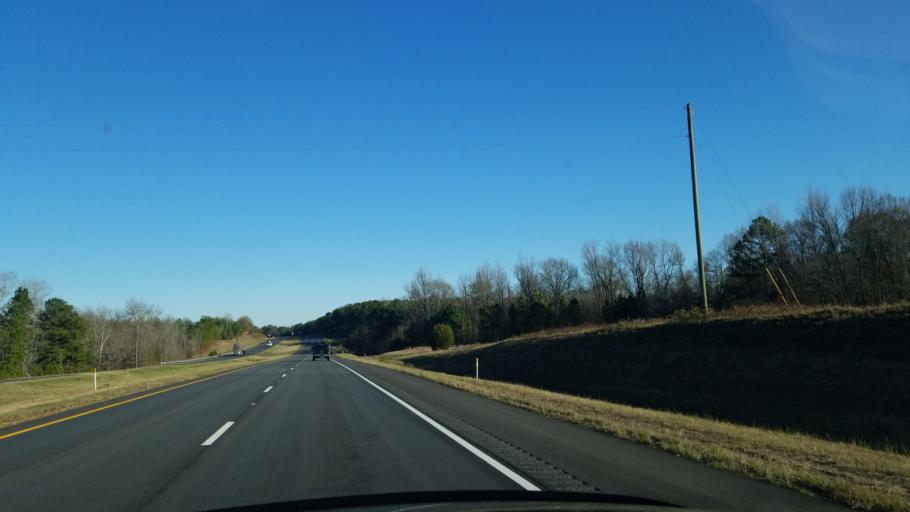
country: US
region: Georgia
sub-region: Talbot County
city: Talbotton
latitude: 32.5634
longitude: -84.6241
